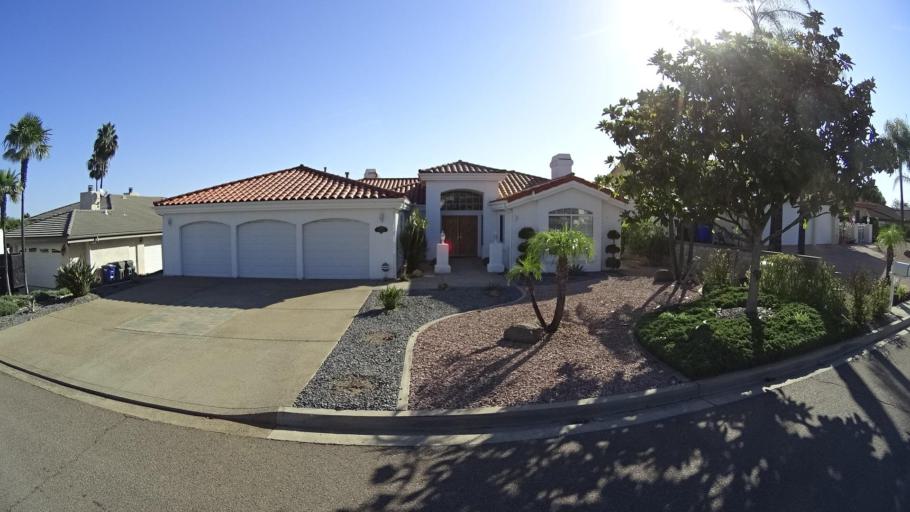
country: US
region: California
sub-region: San Diego County
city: Hidden Meadows
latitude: 33.2199
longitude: -117.1008
